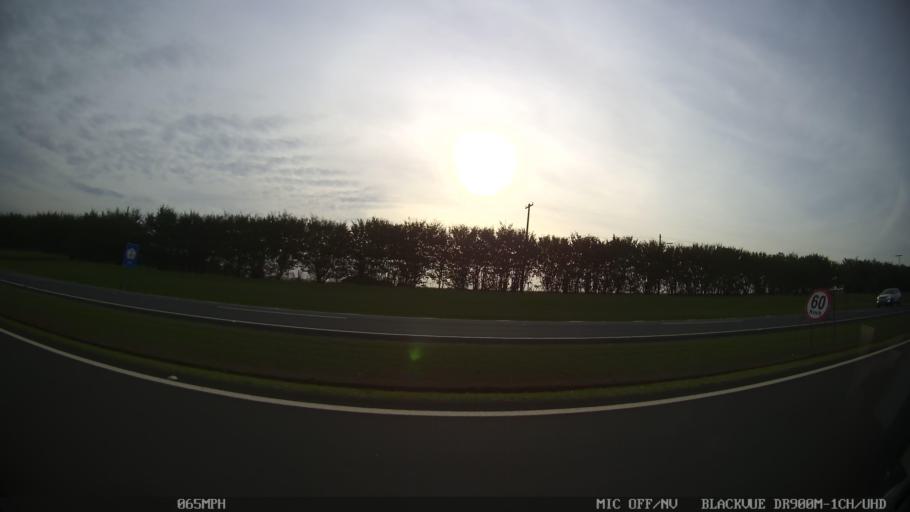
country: BR
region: Sao Paulo
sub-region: Iracemapolis
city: Iracemapolis
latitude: -22.6364
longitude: -47.5078
